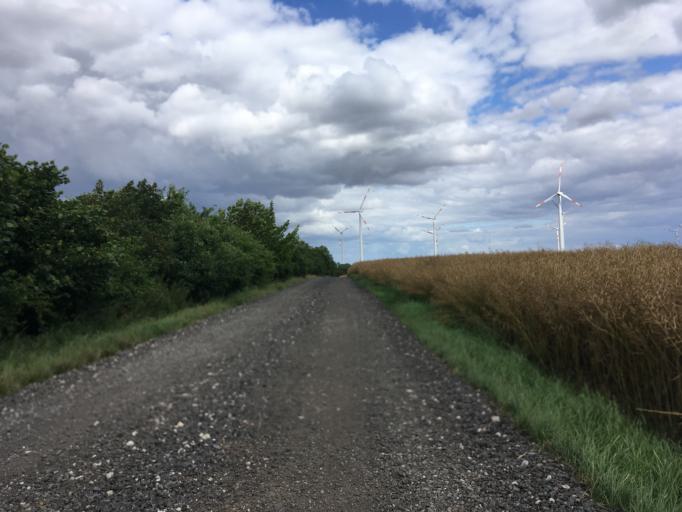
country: DE
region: Brandenburg
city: Gramzow
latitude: 53.2737
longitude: 14.0304
